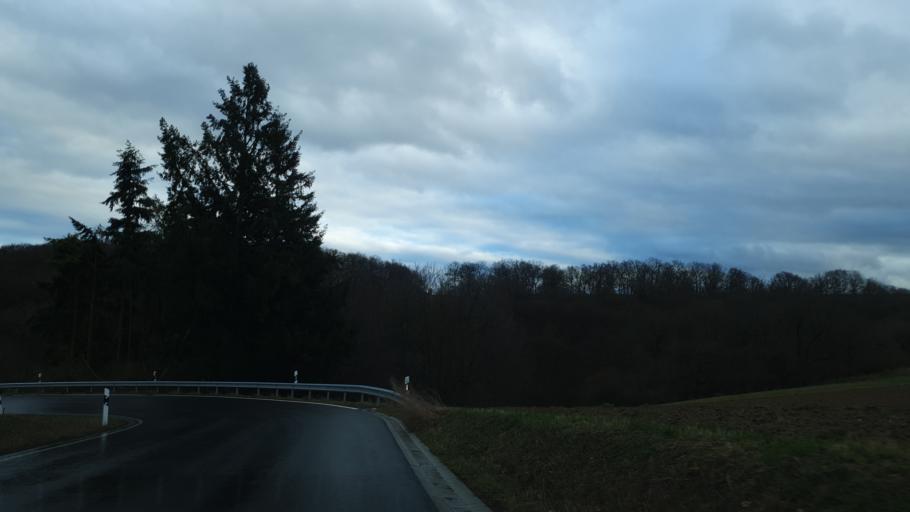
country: DE
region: Rheinland-Pfalz
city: Bremberg
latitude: 50.3032
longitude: 7.9228
